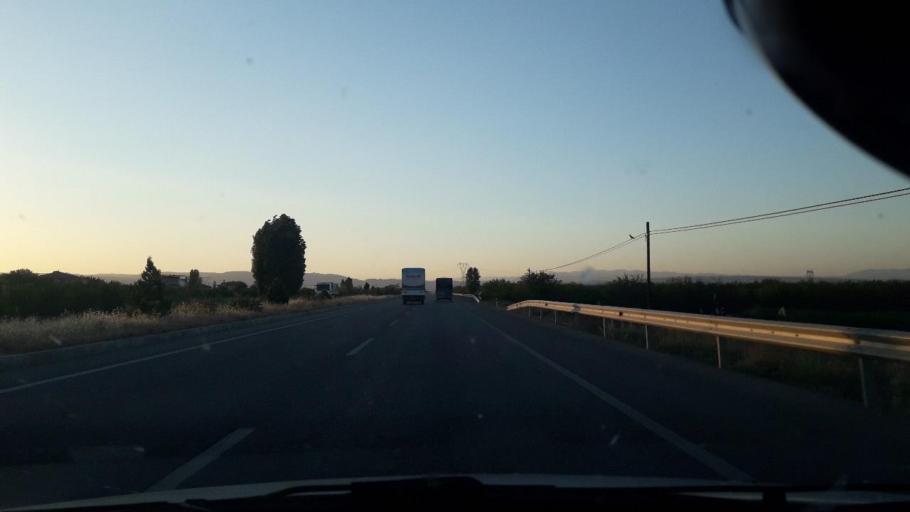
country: TR
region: Malatya
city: Yazihan
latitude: 38.4748
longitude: 38.2230
